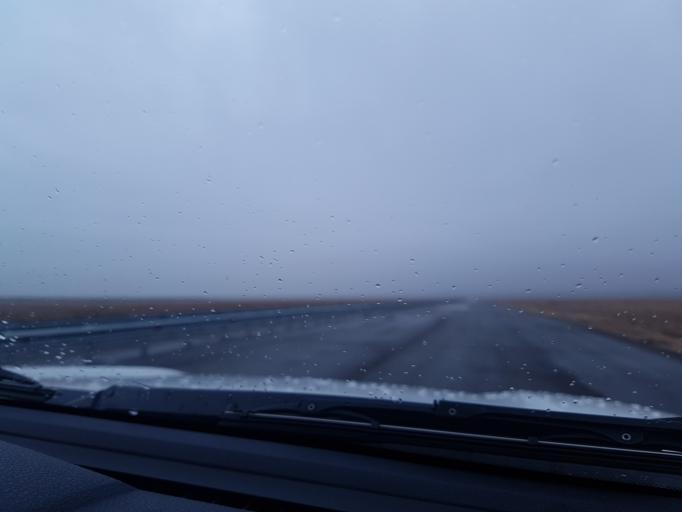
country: TM
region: Balkan
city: Balkanabat
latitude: 39.9556
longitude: 53.8323
